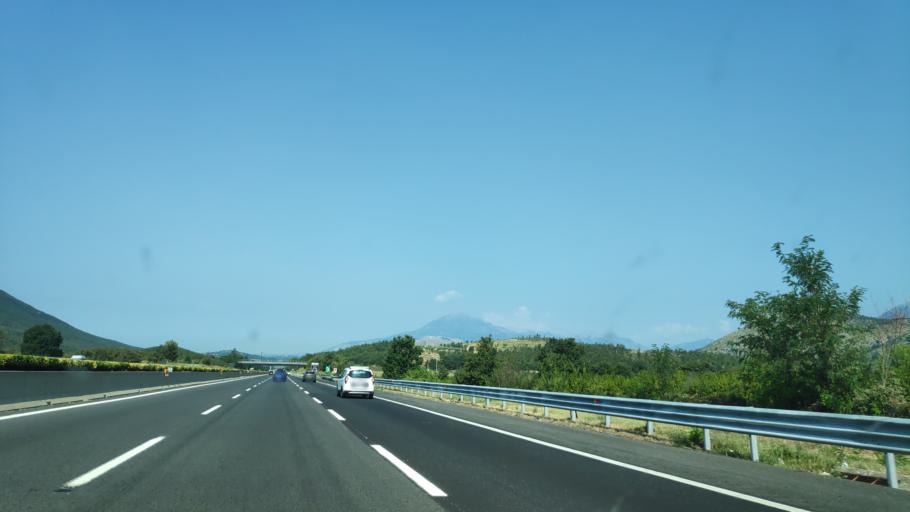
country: IT
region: Campania
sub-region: Provincia di Caserta
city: San Pietro Infine
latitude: 41.4120
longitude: 13.9513
